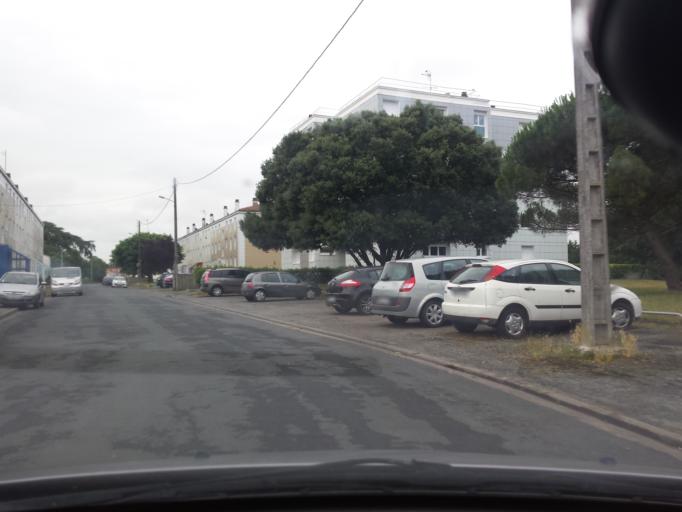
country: FR
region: Pays de la Loire
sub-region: Departement de la Vendee
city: Lucon
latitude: 46.4620
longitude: -1.1709
